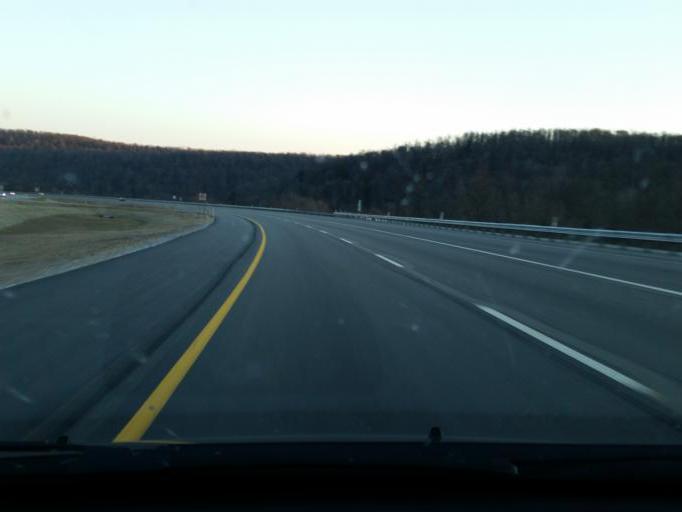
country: US
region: Pennsylvania
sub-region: Somerset County
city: Somerset
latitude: 40.0931
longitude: -79.2029
